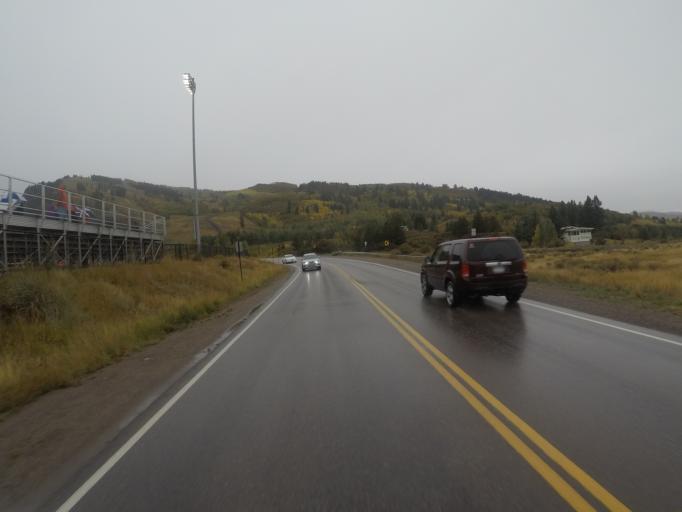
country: US
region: Colorado
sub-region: Pitkin County
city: Aspen
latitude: 39.1932
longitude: -106.8488
